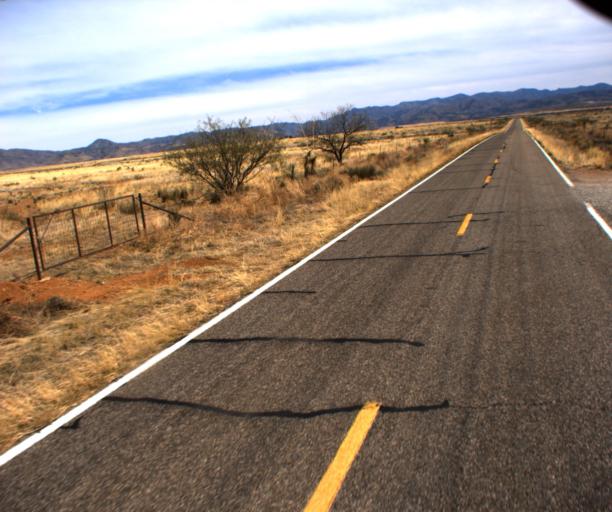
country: US
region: Arizona
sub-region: Cochise County
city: Willcox
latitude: 32.0427
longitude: -109.4837
